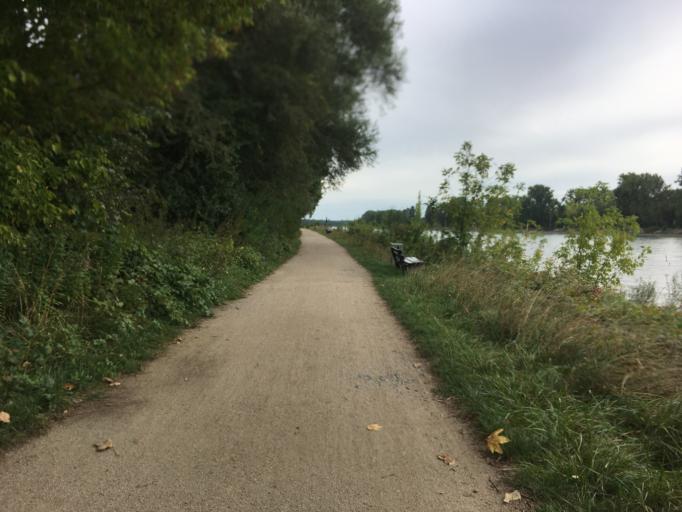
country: DE
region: Rheinland-Pfalz
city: Altrip
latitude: 49.4015
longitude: 8.4981
